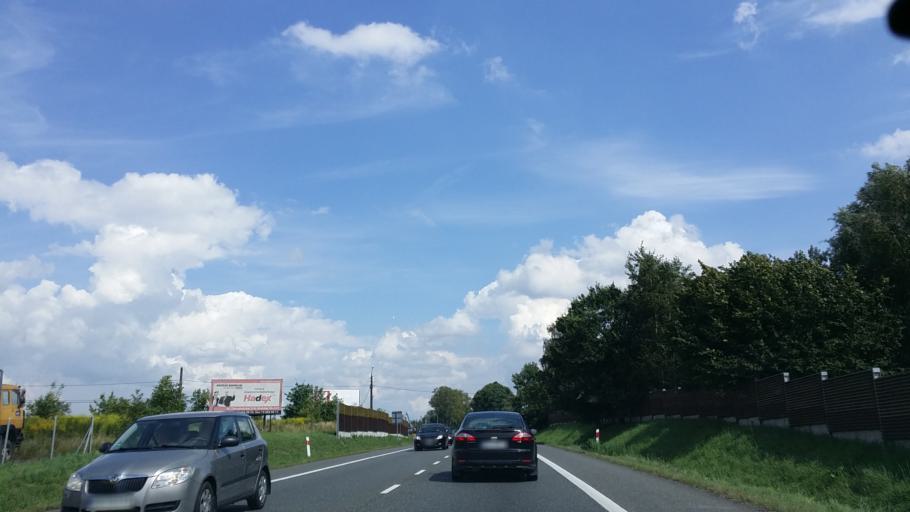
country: PL
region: Lesser Poland Voivodeship
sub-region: Powiat wielicki
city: Wieliczka
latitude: 49.9948
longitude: 20.0594
